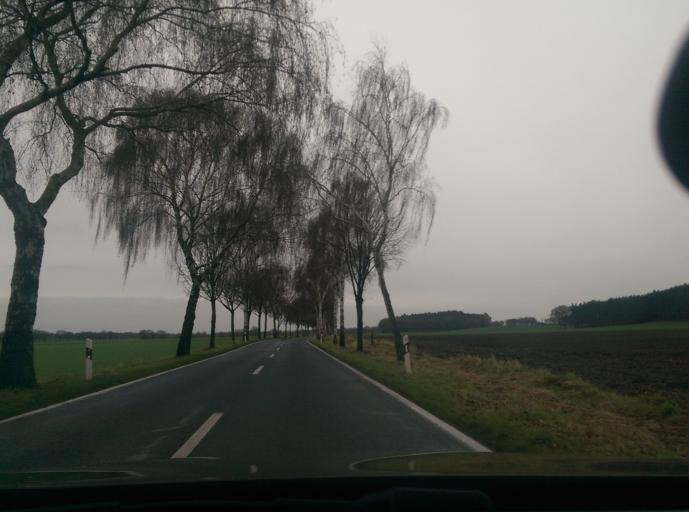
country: DE
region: Lower Saxony
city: Lindwedel
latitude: 52.5804
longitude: 9.6682
